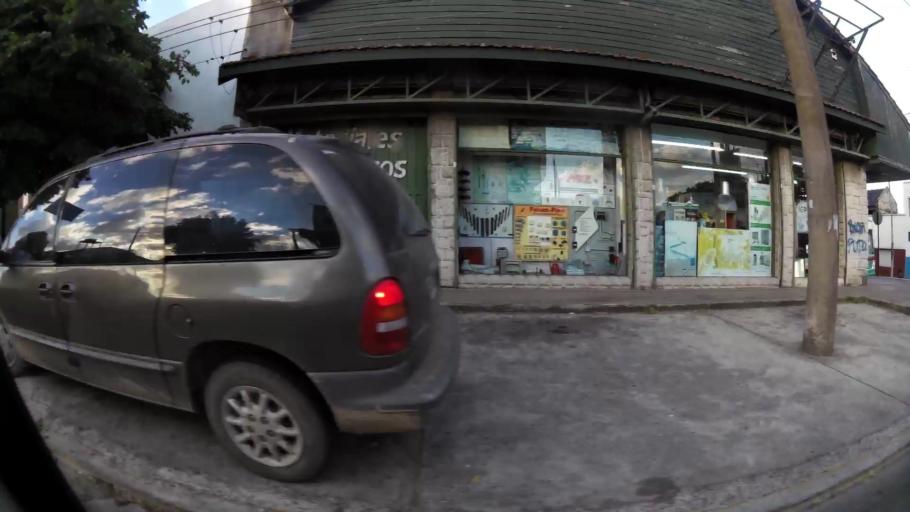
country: AR
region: Buenos Aires
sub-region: Partido de La Plata
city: La Plata
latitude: -34.8920
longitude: -57.9474
